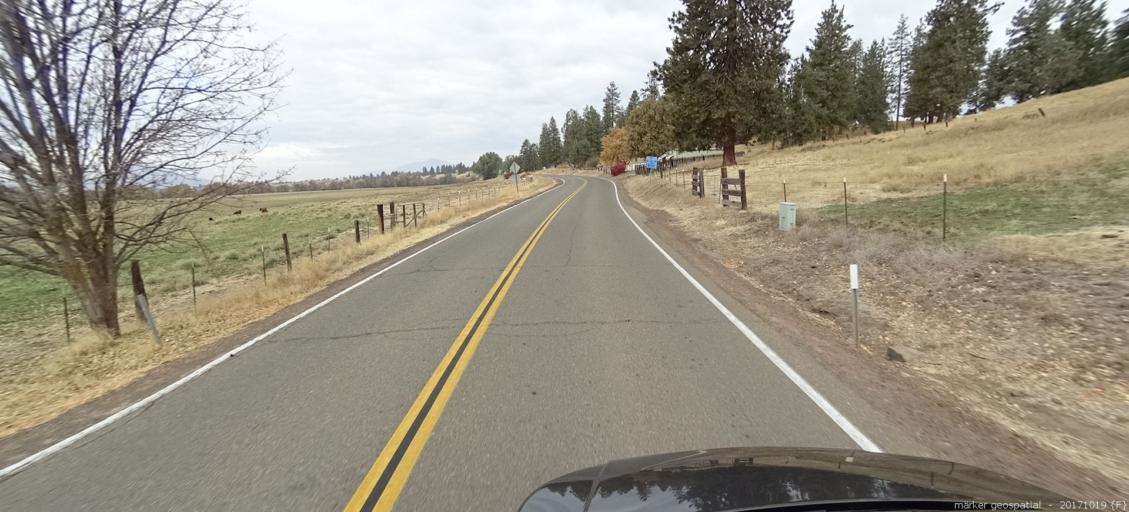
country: US
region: California
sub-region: Shasta County
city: Burney
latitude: 41.0540
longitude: -121.3601
